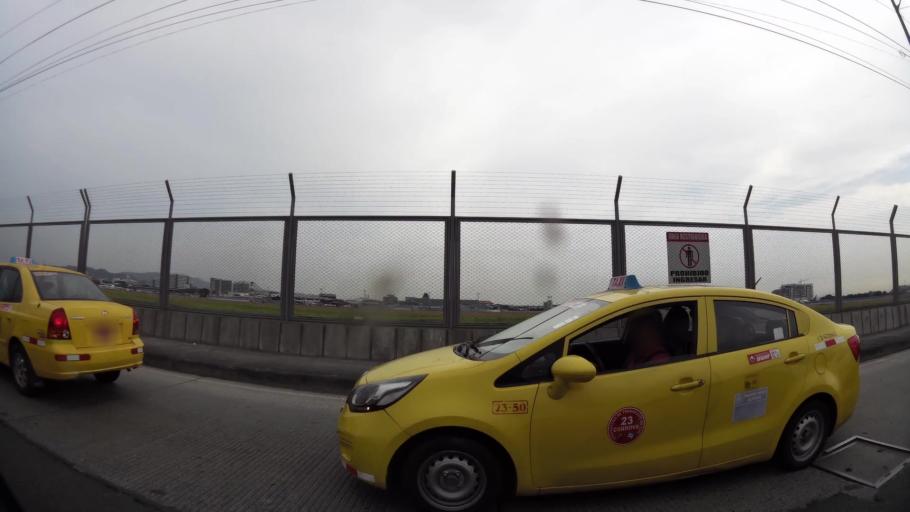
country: EC
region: Guayas
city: Eloy Alfaro
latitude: -2.1540
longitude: -79.8790
